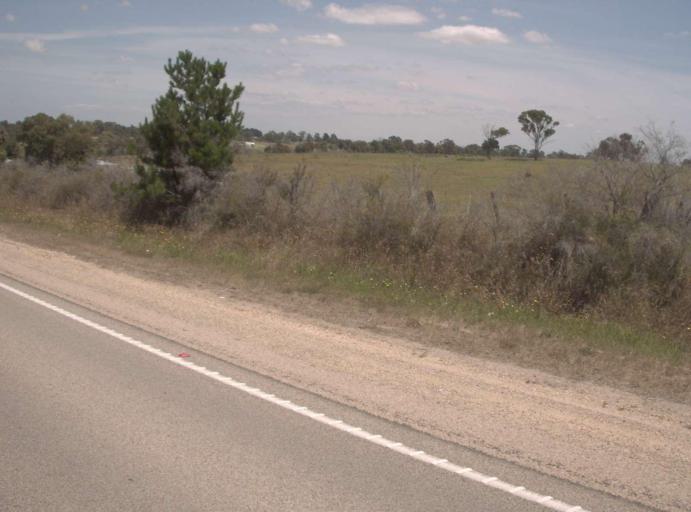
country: AU
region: Victoria
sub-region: East Gippsland
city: Bairnsdale
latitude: -37.7856
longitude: 147.6811
